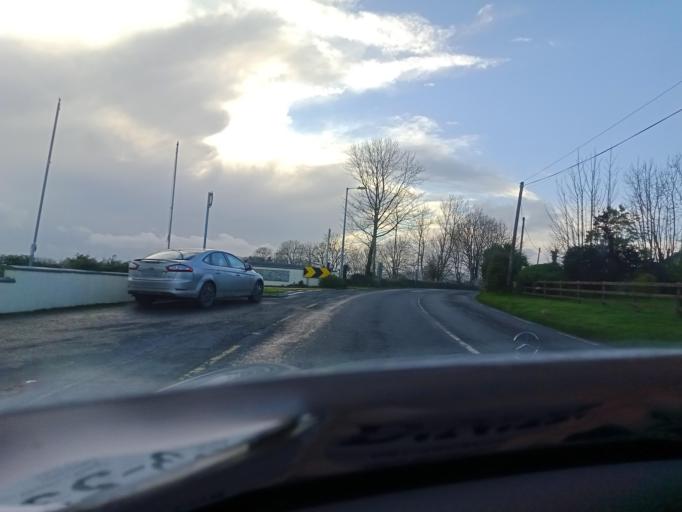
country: IE
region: Munster
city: Carrick-on-Suir
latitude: 52.3318
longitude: -7.4042
